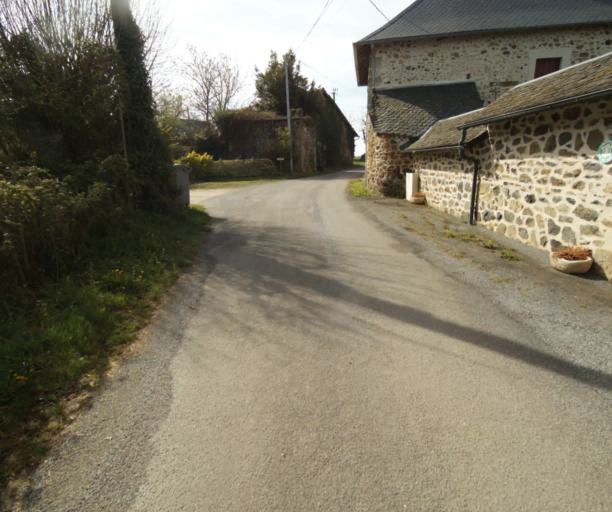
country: FR
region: Limousin
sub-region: Departement de la Correze
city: Laguenne
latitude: 45.2618
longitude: 1.8061
